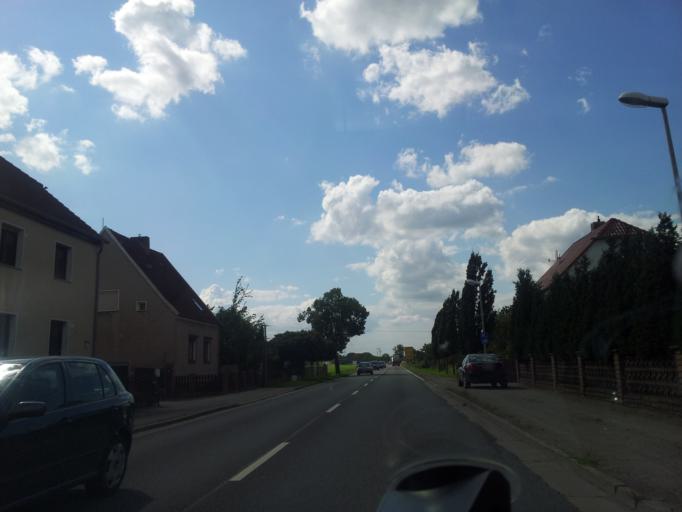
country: DE
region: Saxony-Anhalt
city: Haldensleben I
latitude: 52.2723
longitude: 11.4590
